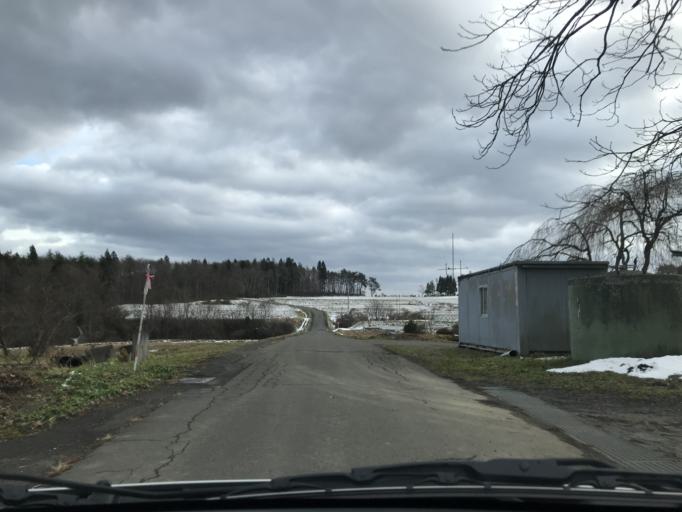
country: JP
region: Iwate
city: Ichinoseki
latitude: 38.9907
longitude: 141.0007
